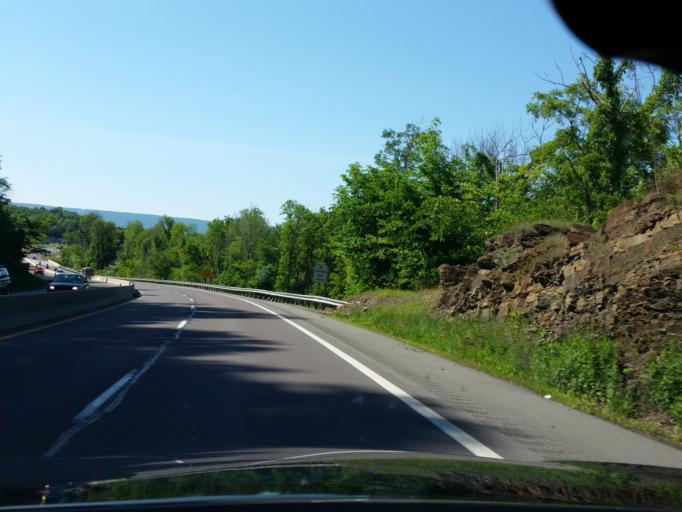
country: US
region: Pennsylvania
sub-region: Northumberland County
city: Dewart
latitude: 41.0983
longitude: -76.8883
